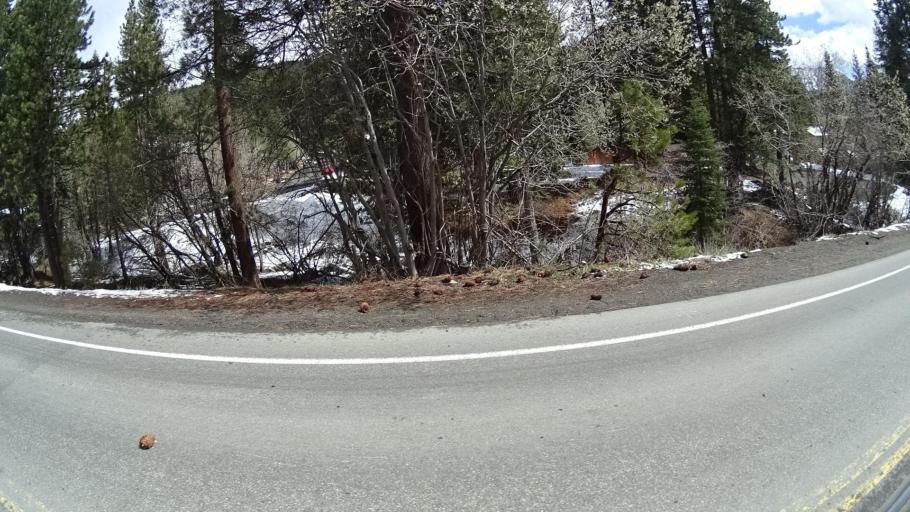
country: US
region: Nevada
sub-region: Washoe County
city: Incline Village
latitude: 39.2665
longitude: -119.9455
